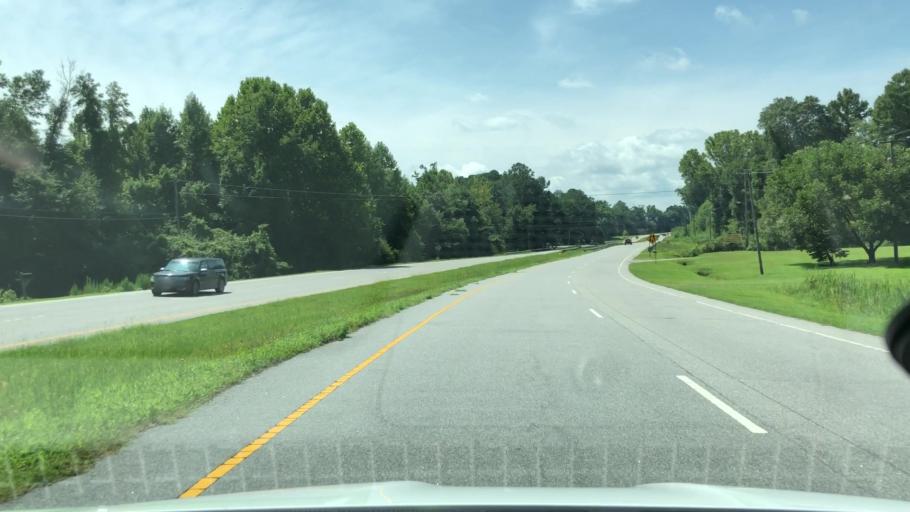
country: US
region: North Carolina
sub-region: Martin County
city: Williamston
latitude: 35.7909
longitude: -77.0593
